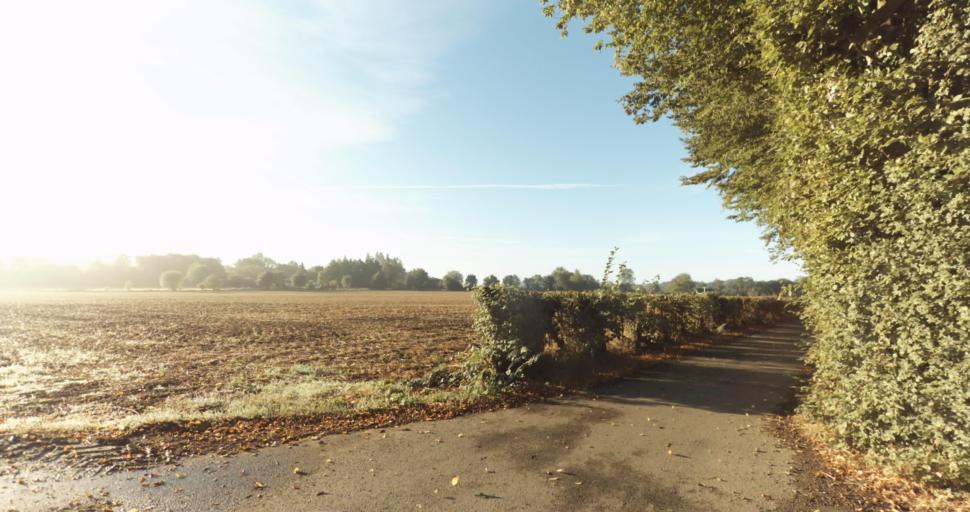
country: FR
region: Lower Normandy
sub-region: Departement de l'Orne
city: Vimoutiers
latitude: 48.9150
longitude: 0.1537
